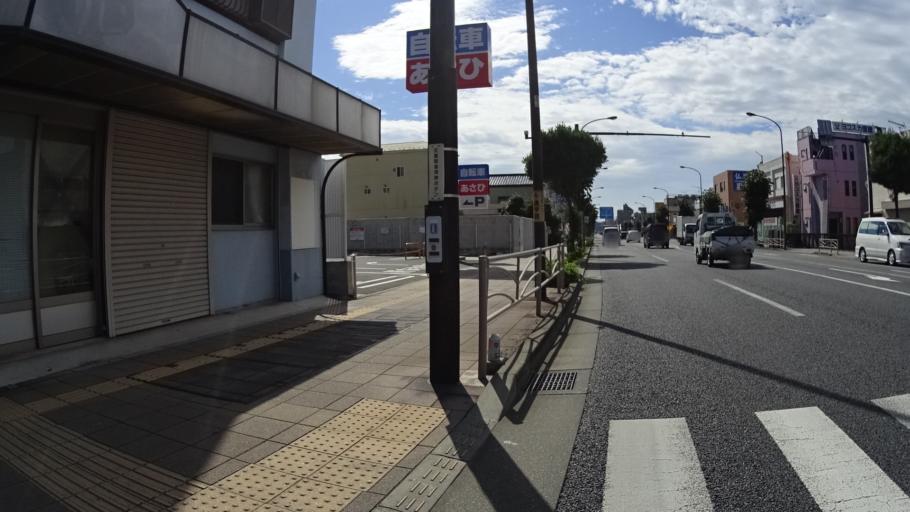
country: JP
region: Kanagawa
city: Yokosuka
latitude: 35.2697
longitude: 139.6807
